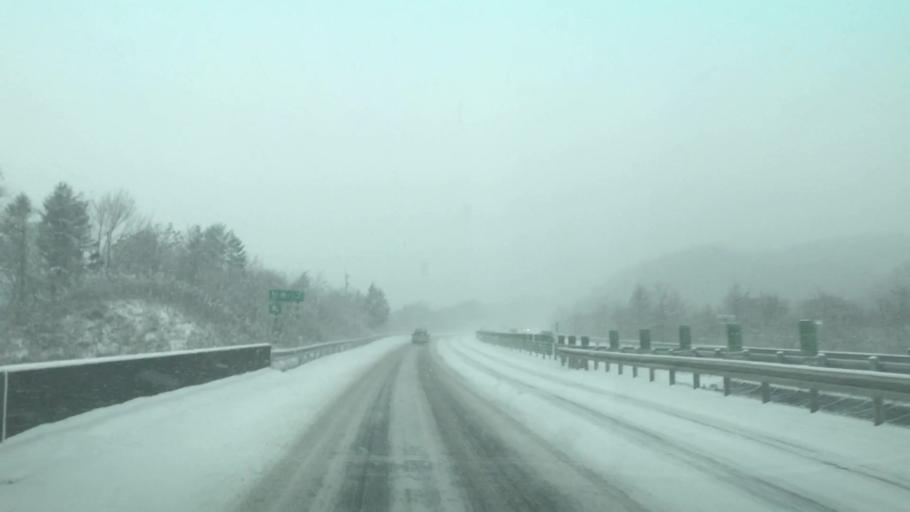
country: JP
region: Hokkaido
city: Shiraoi
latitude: 42.5007
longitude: 141.2642
